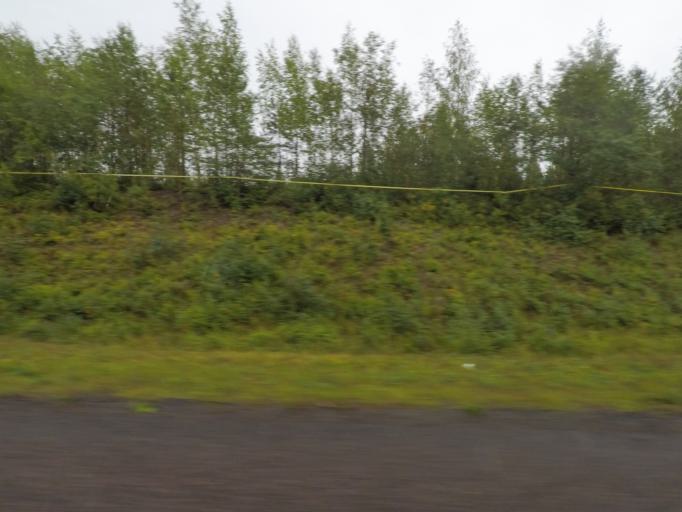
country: FI
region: Northern Savo
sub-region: Varkaus
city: Varkaus
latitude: 62.3917
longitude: 27.8149
